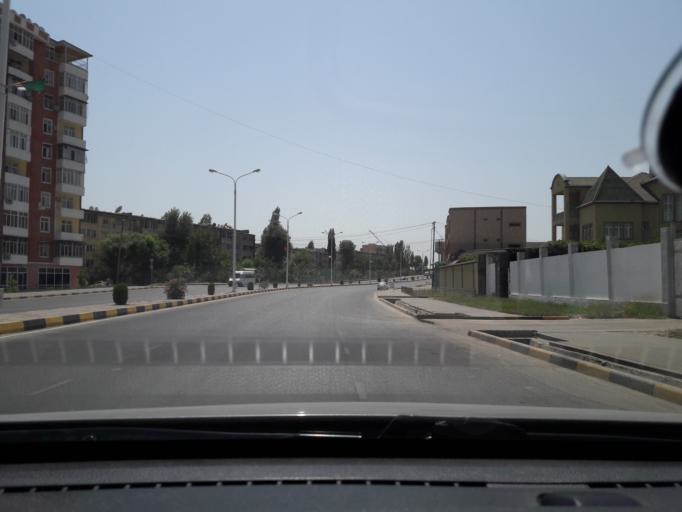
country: TJ
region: Dushanbe
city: Dushanbe
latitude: 38.5858
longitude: 68.7131
